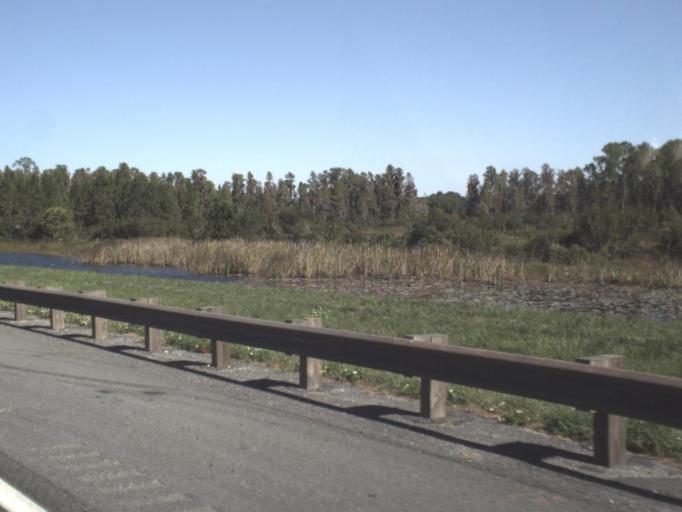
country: US
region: Florida
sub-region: Hillsborough County
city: Cheval
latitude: 28.1735
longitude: -82.5359
